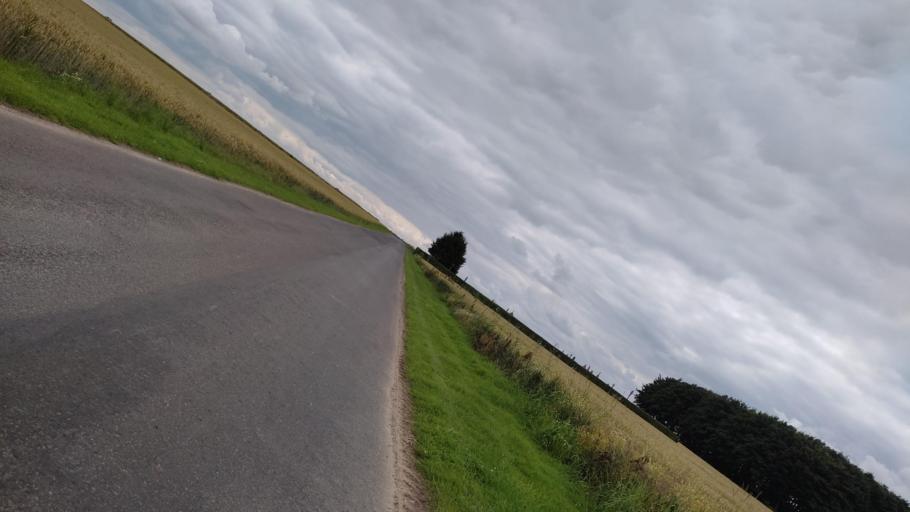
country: FR
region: Nord-Pas-de-Calais
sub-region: Departement du Pas-de-Calais
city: Beaumetz-les-Loges
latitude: 50.2356
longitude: 2.6298
